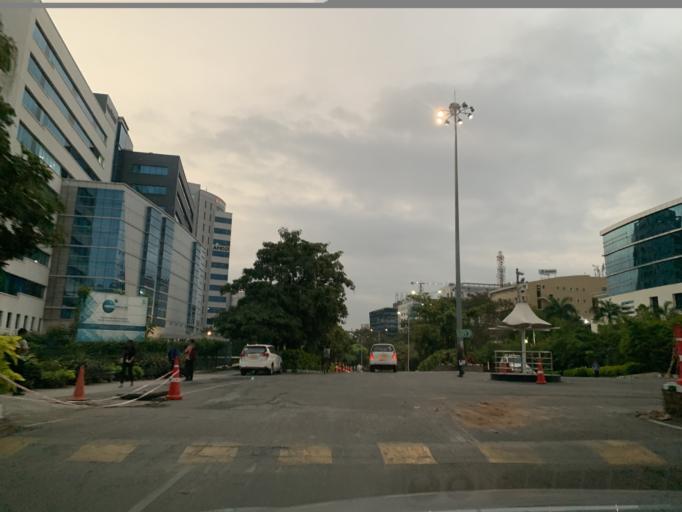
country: IN
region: Telangana
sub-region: Rangareddi
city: Kukatpalli
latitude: 17.4394
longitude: 78.3803
